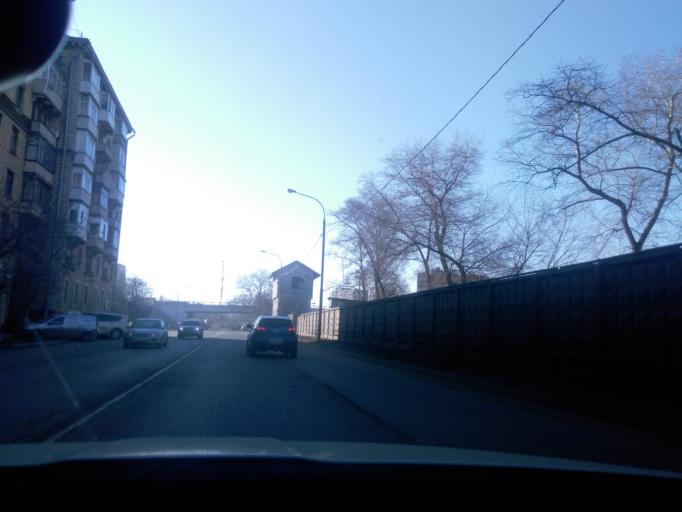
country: RU
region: Moscow
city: Sokol
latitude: 55.7997
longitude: 37.4993
